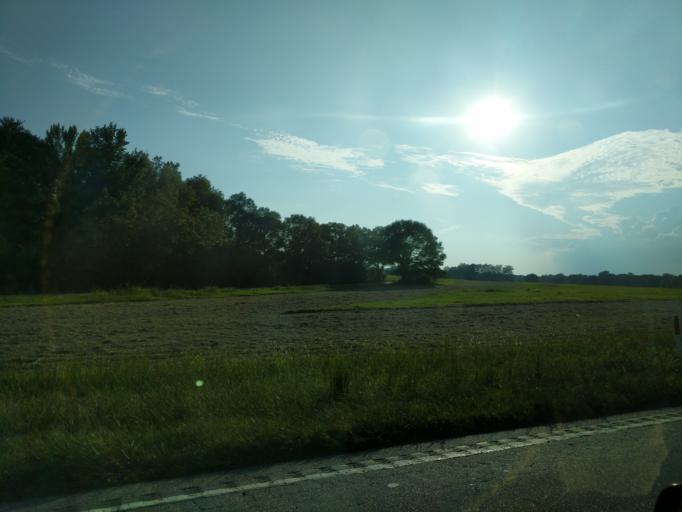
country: US
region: South Carolina
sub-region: Anderson County
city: Williamston
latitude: 34.6492
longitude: -82.4844
